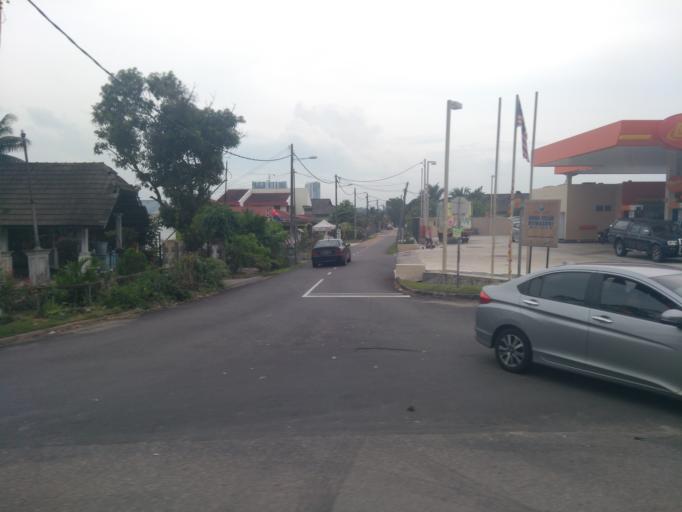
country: MY
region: Johor
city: Skudai
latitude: 1.4981
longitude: 103.6992
